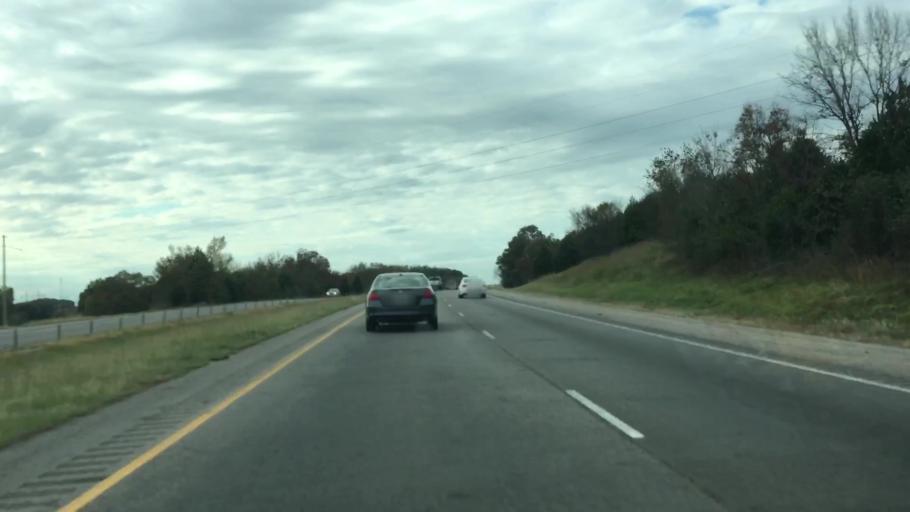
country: US
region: Arkansas
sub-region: Conway County
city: Morrilton
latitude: 35.1641
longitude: -92.6797
